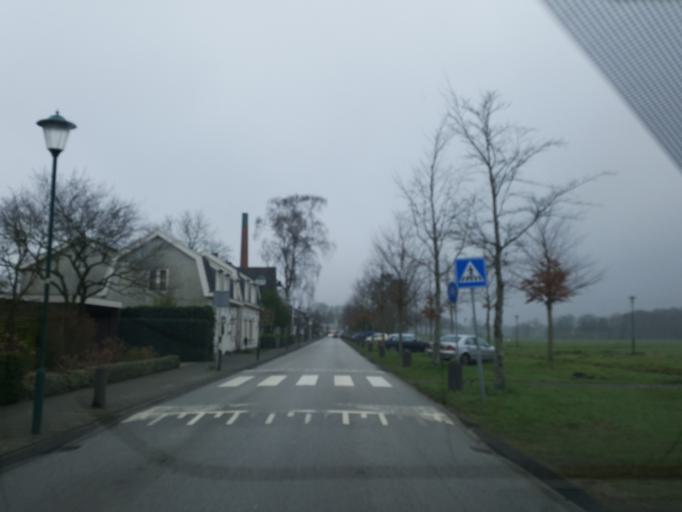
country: NL
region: North Holland
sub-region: Gemeente Wijdemeren
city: Kortenhoef
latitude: 52.2567
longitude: 5.1212
